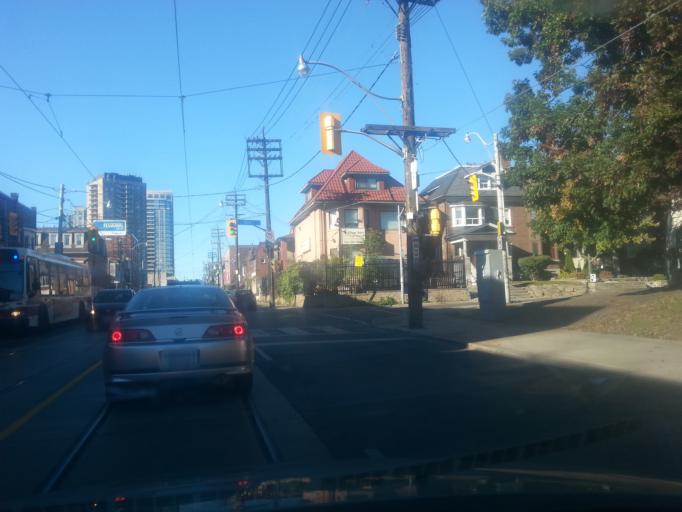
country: CA
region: Ontario
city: Toronto
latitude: 43.6795
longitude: -79.4169
